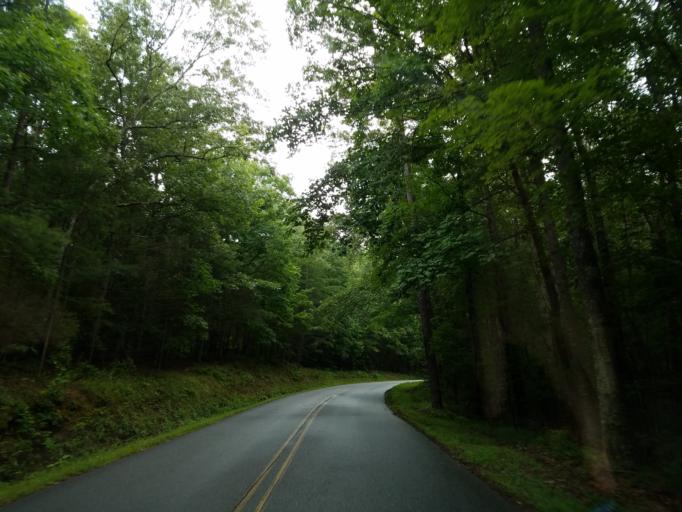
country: US
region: Georgia
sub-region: Fannin County
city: Blue Ridge
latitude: 34.8061
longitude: -84.2761
